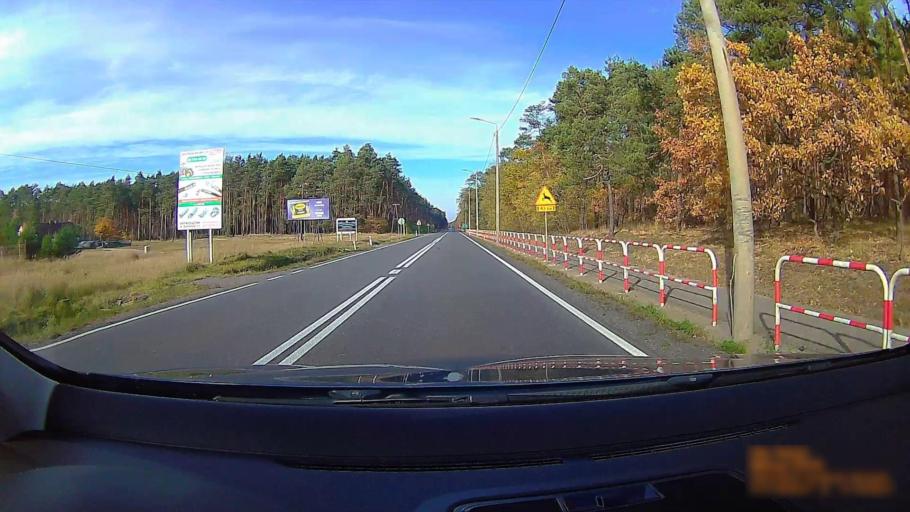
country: PL
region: Greater Poland Voivodeship
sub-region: Powiat ostrzeszowski
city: Ostrzeszow
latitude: 51.4463
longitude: 17.9109
